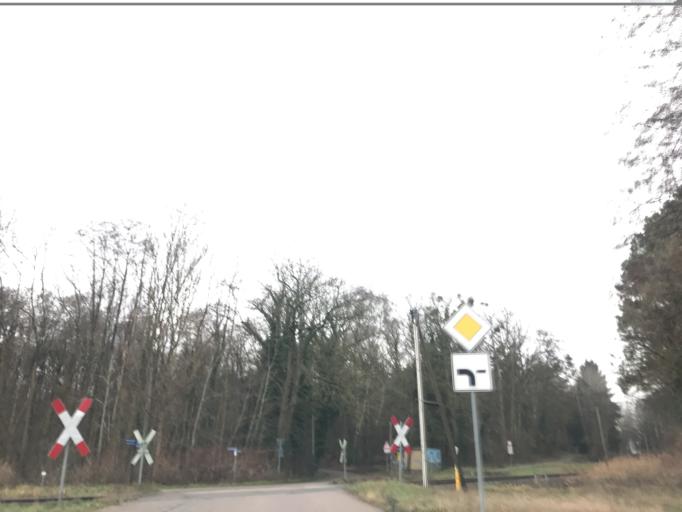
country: DE
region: Brandenburg
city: Lindow
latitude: 52.9784
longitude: 12.9817
